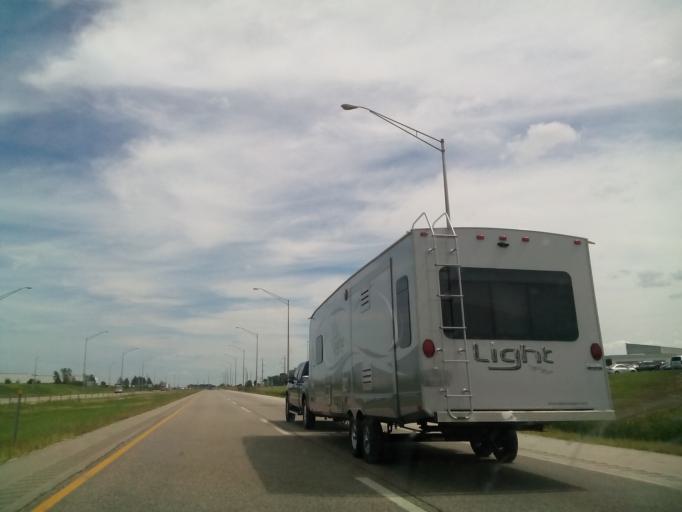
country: US
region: Illinois
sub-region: DeKalb County
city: DeKalb
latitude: 41.9016
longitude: -88.7408
